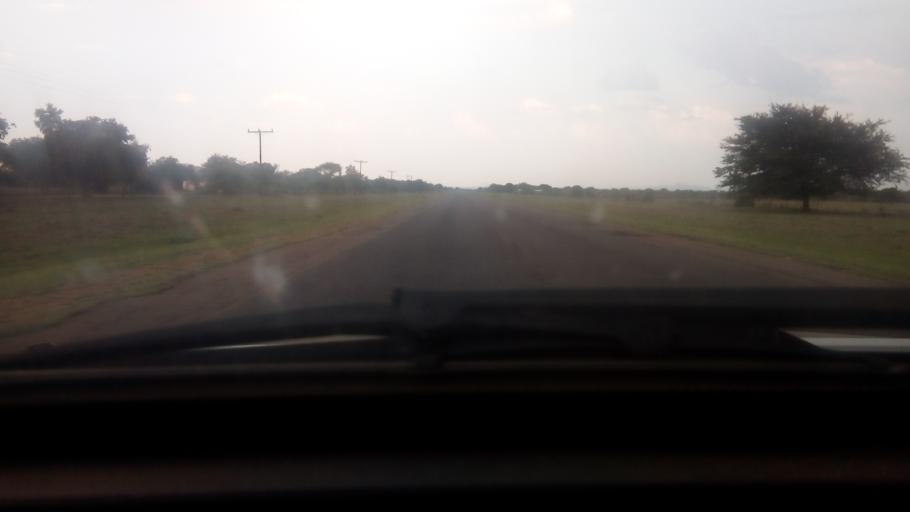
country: BW
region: Kweneng
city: Metsemotlhaba
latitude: -24.4922
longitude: 25.7440
